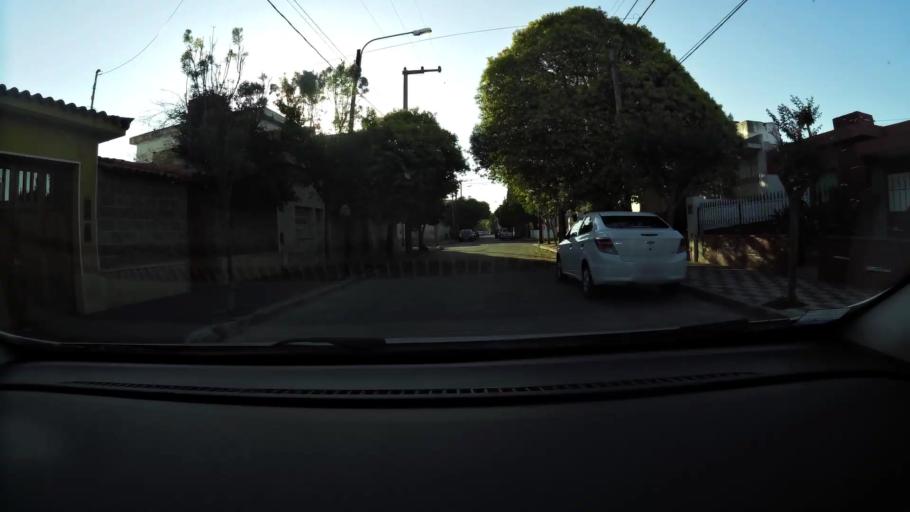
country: AR
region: Cordoba
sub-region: Departamento de Capital
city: Cordoba
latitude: -31.3715
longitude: -64.2075
